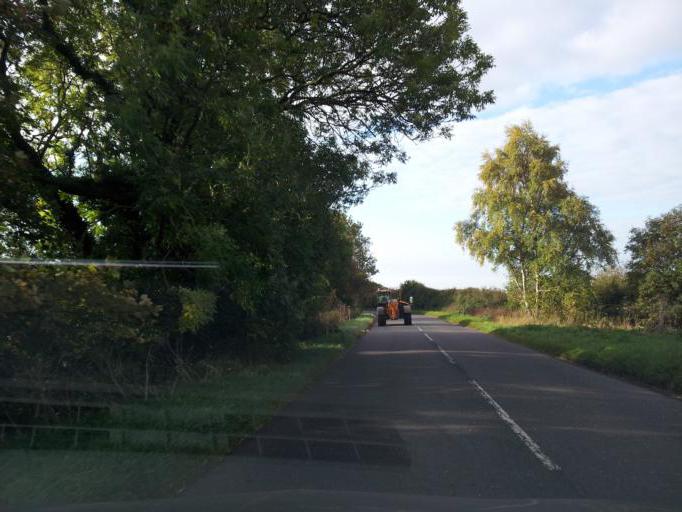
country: GB
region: England
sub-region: Lincolnshire
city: Long Bennington
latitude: 52.9836
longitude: -0.8054
